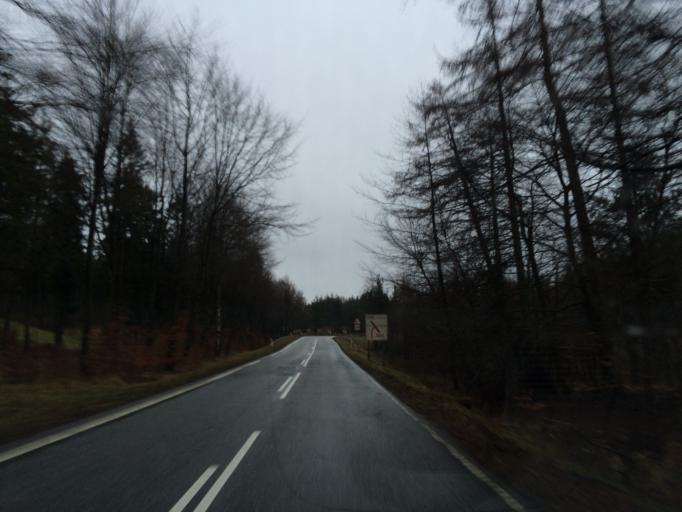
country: DK
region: North Denmark
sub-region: Rebild Kommune
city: Stovring
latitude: 56.8218
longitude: 9.8192
